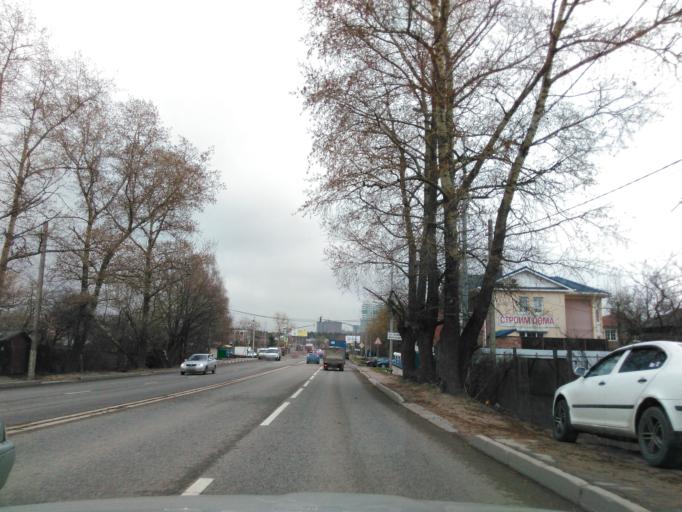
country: RU
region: Moskovskaya
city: Opalikha
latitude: 55.8393
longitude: 37.2500
